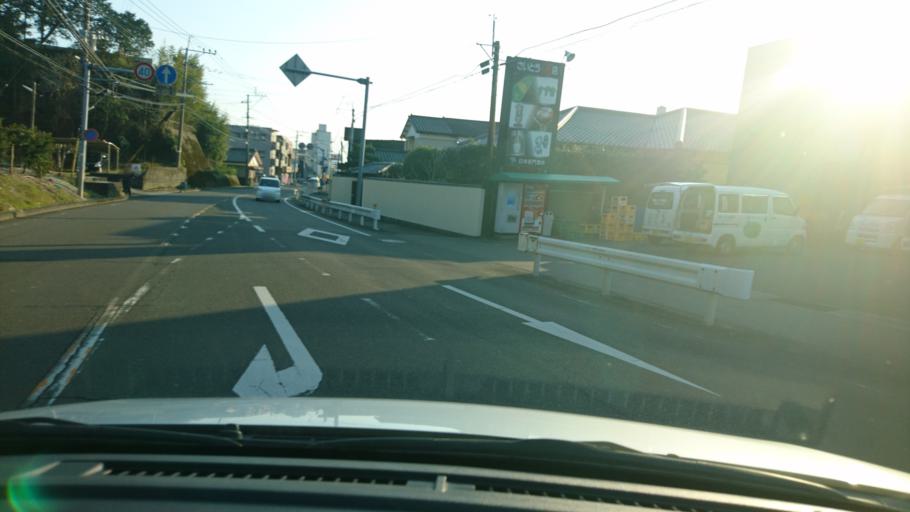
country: JP
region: Miyazaki
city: Miyazaki-shi
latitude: 31.9667
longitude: 131.4403
